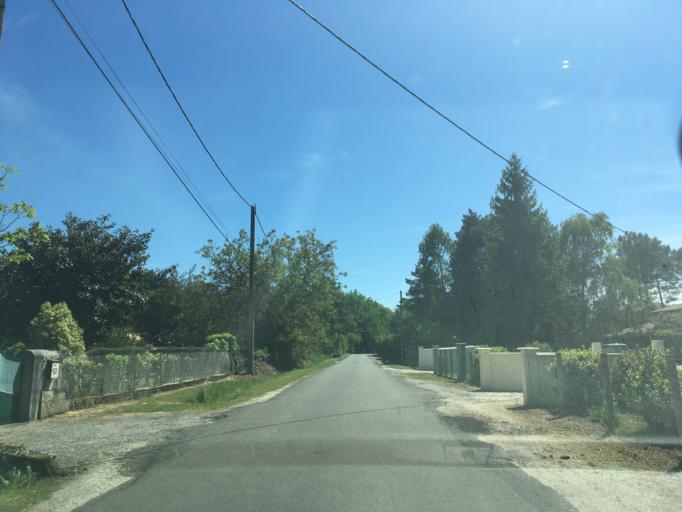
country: FR
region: Aquitaine
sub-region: Departement de la Gironde
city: Lesparre-Medoc
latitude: 45.2942
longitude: -0.8928
